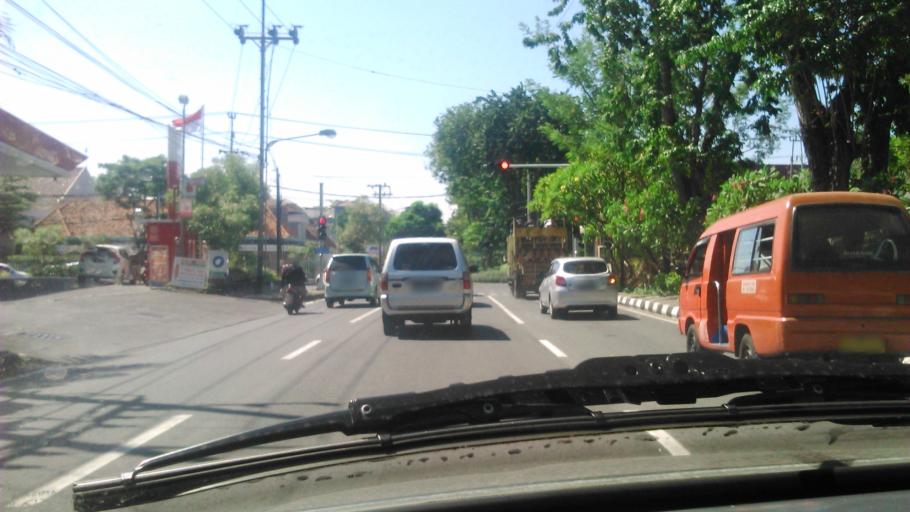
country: ID
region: East Java
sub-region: Kota Surabaya
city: Surabaya
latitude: -7.2565
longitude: 112.7467
